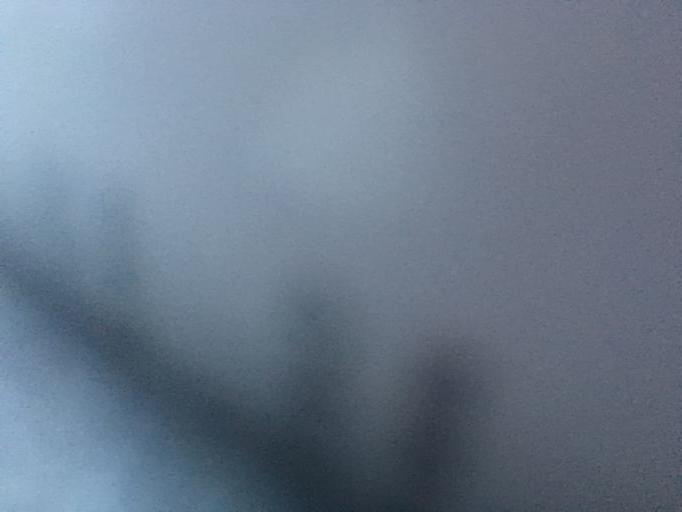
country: KZ
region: Astana Qalasy
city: Astana
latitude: 51.1299
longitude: 71.4397
